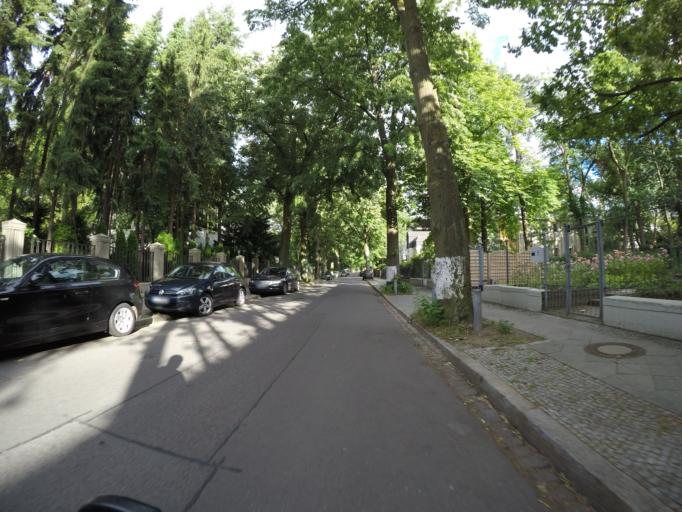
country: DE
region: Berlin
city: Grunewald
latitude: 52.4838
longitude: 13.2784
